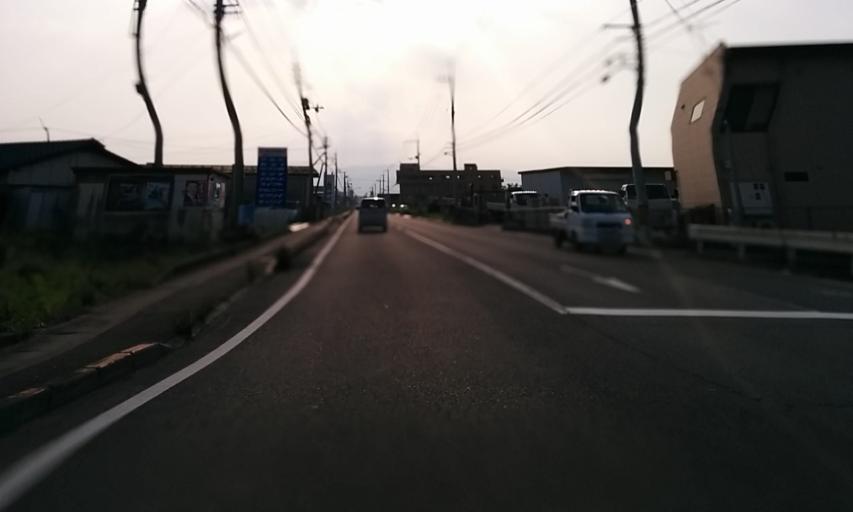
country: JP
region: Ehime
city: Saijo
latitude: 33.8946
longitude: 133.1565
